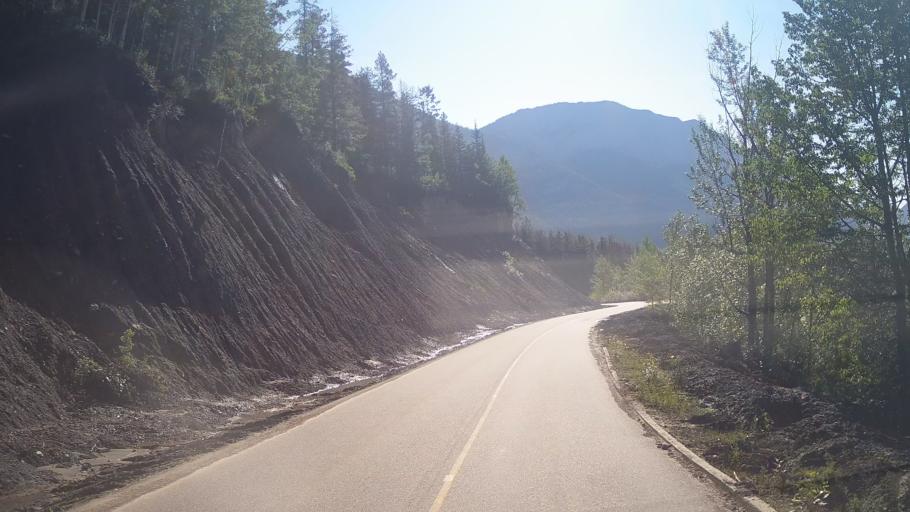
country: CA
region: Alberta
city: Hinton
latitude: 53.1778
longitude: -117.8484
